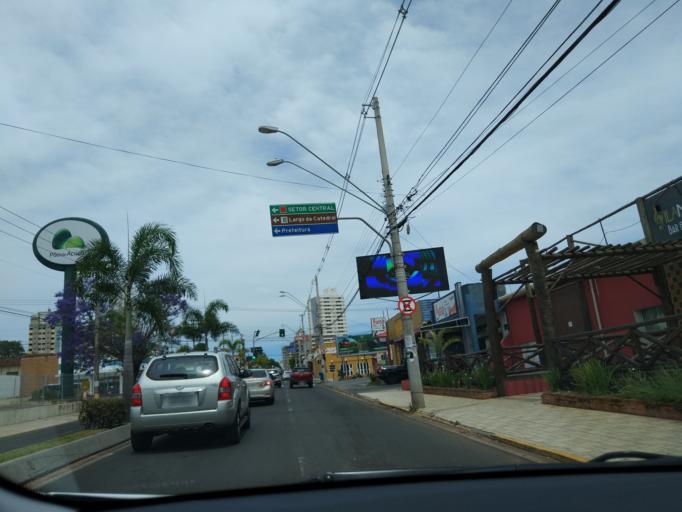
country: BR
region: Sao Paulo
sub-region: Botucatu
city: Botucatu
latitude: -22.8825
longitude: -48.4522
